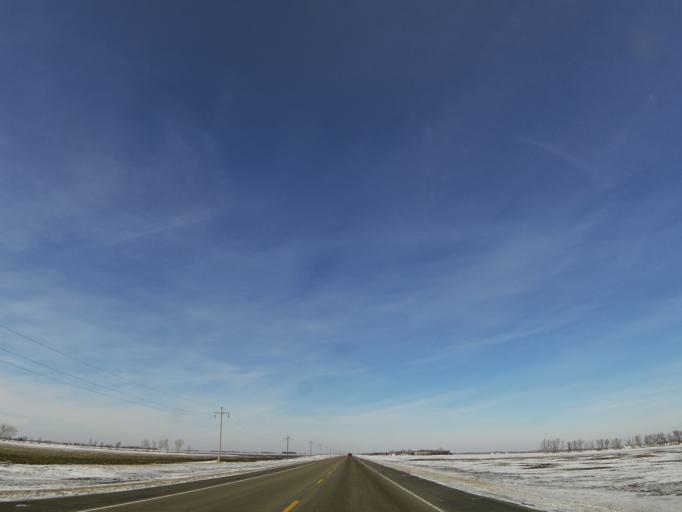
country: US
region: North Dakota
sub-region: Walsh County
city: Grafton
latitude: 48.4121
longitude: -97.2391
